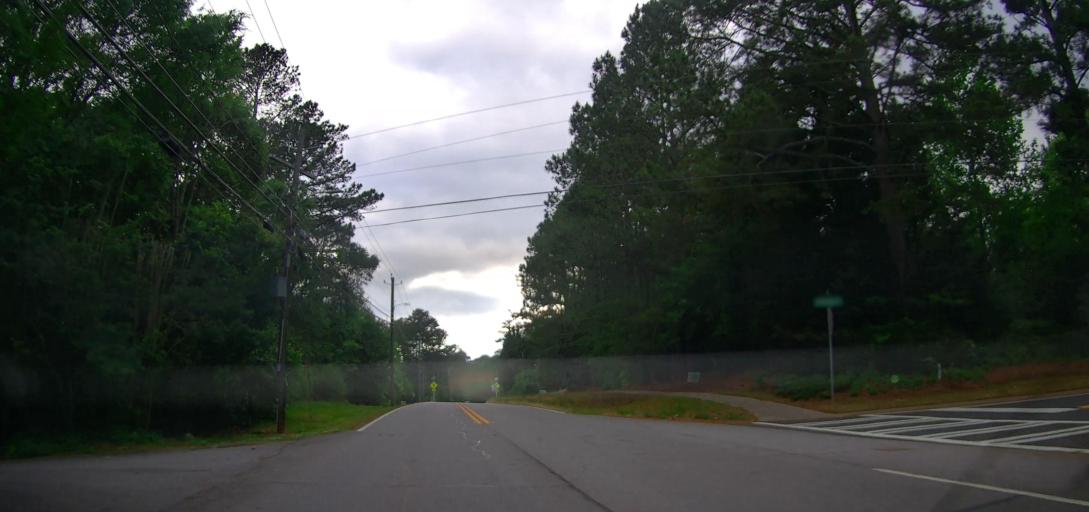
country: US
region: Georgia
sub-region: Clarke County
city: Athens
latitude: 33.9331
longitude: -83.4239
